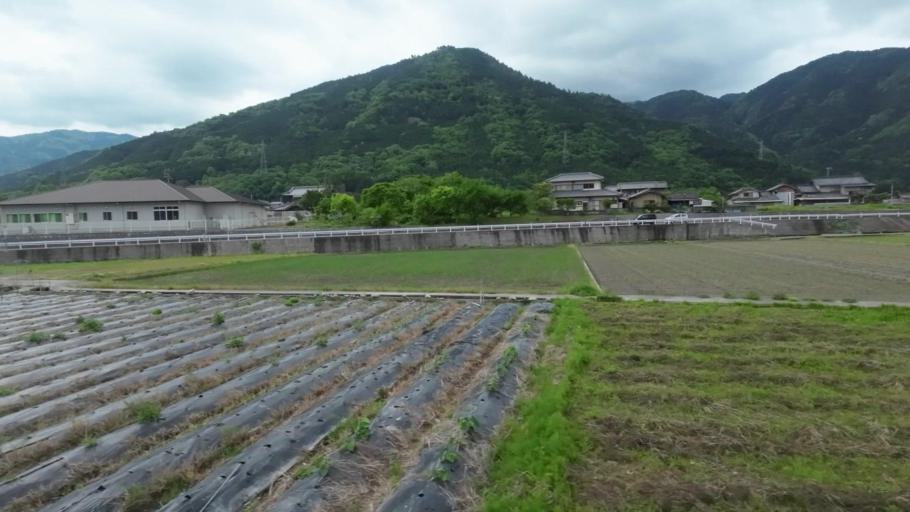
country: JP
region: Tokushima
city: Ikedacho
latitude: 34.0370
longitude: 133.9223
